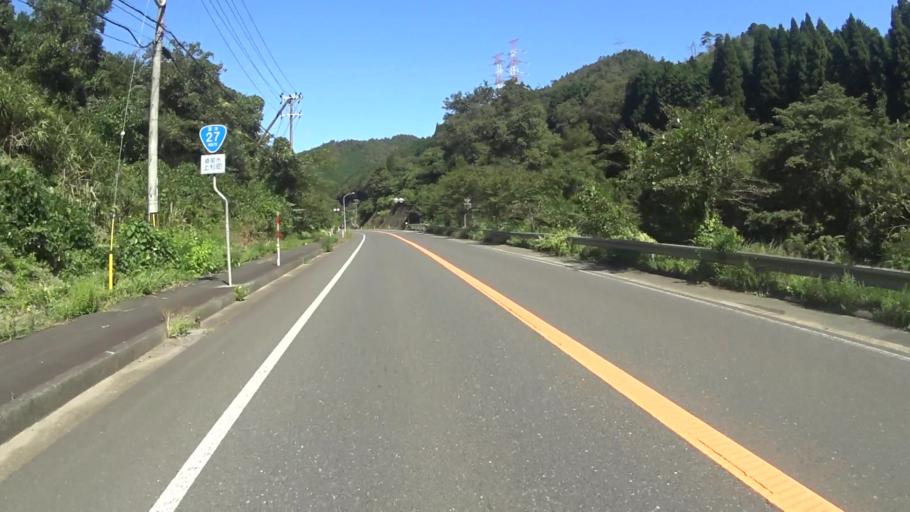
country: JP
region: Kyoto
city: Maizuru
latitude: 35.3726
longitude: 135.3213
